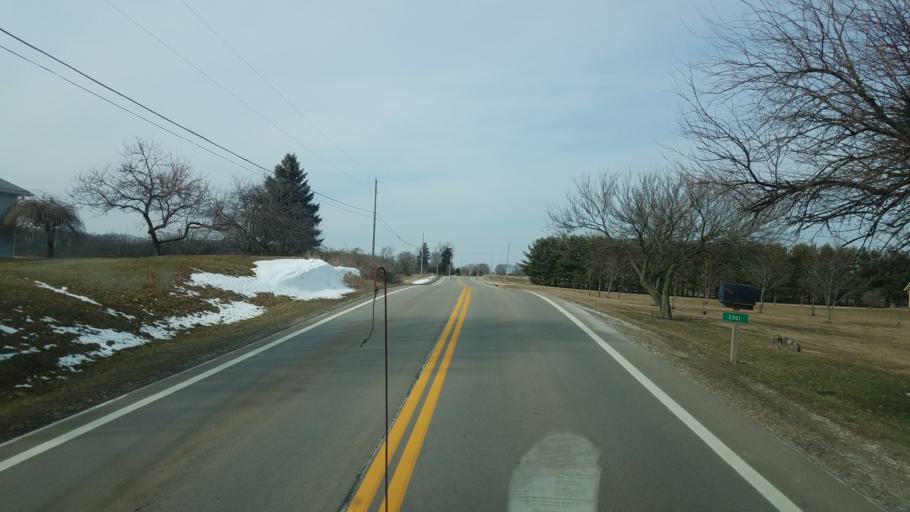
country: US
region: Ohio
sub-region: Delaware County
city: Delaware
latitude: 40.3514
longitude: -83.1396
